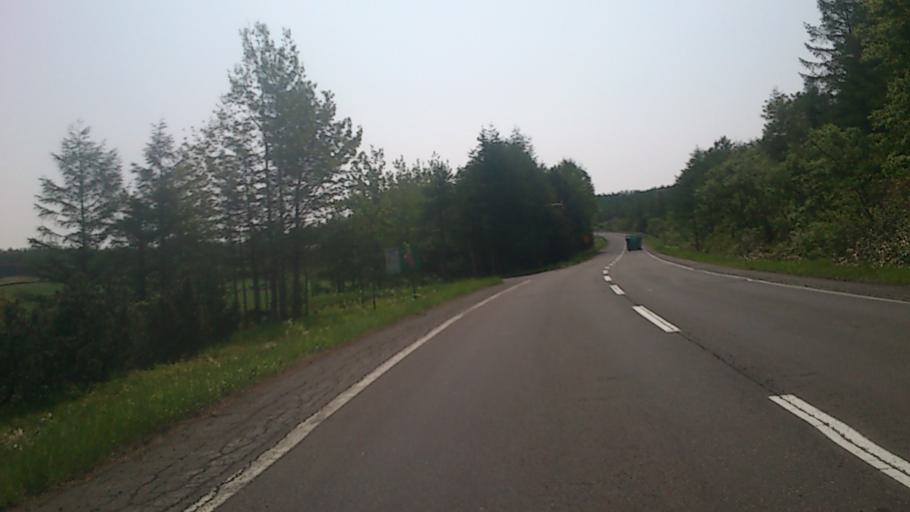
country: JP
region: Hokkaido
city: Kushiro
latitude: 43.4839
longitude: 144.5356
